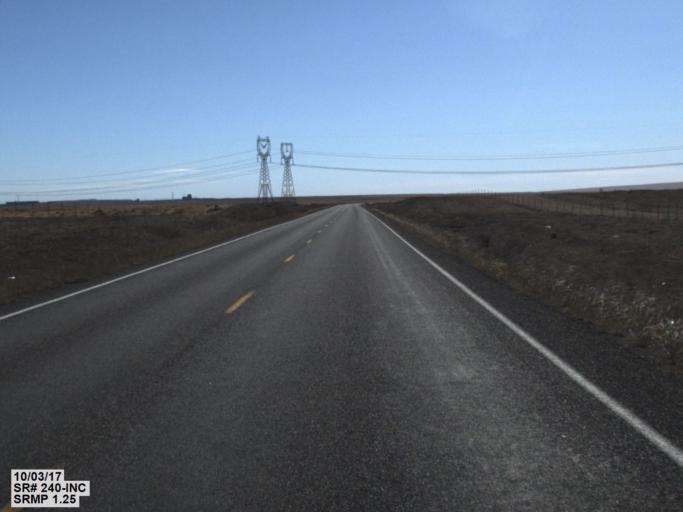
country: US
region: Washington
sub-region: Grant County
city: Desert Aire
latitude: 46.5634
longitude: -119.7146
